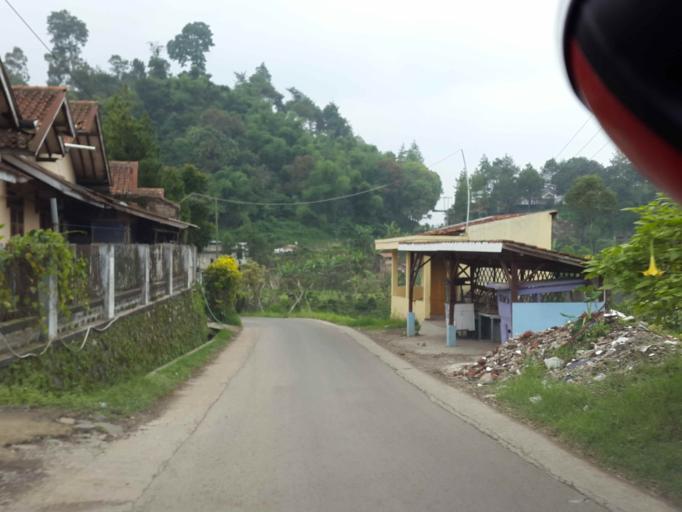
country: ID
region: West Java
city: Lembang
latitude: -6.8169
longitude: 107.5877
